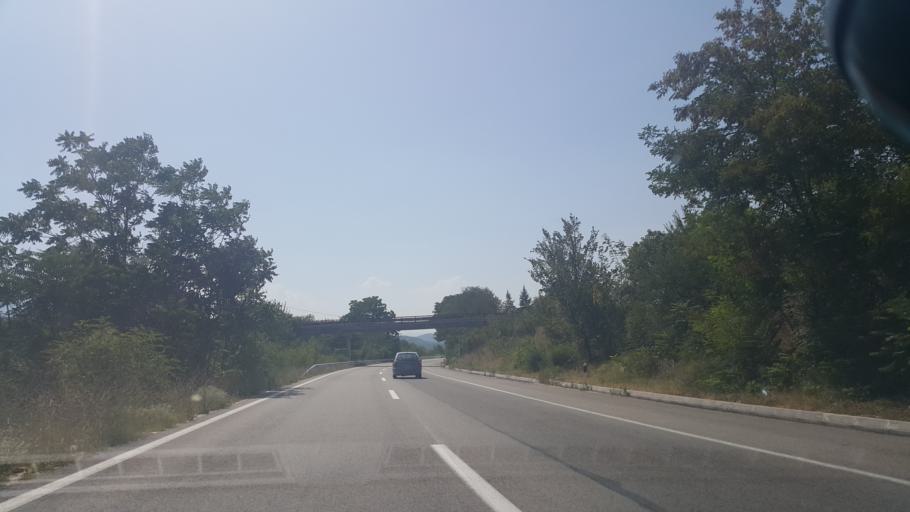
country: MK
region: Petrovec
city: Sredno Konjare
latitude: 41.8948
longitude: 21.6760
